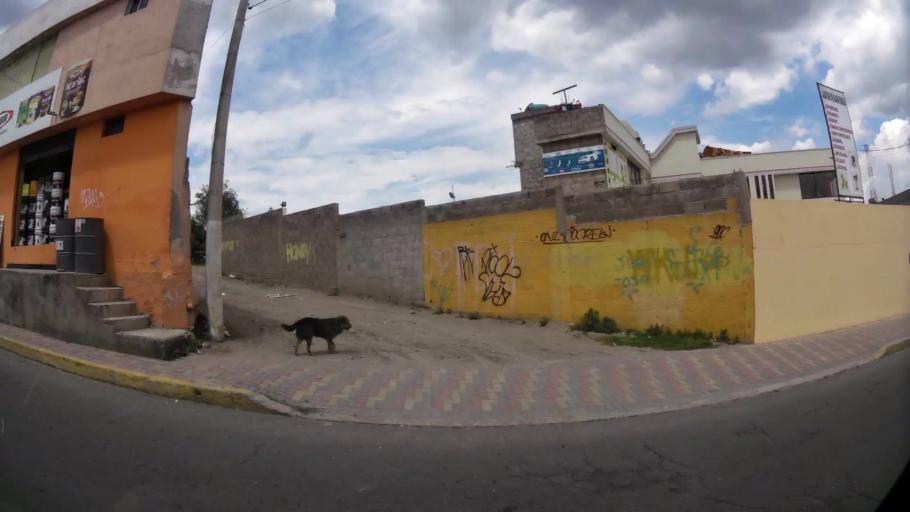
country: EC
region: Pichincha
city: Quito
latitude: -0.0981
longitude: -78.4430
